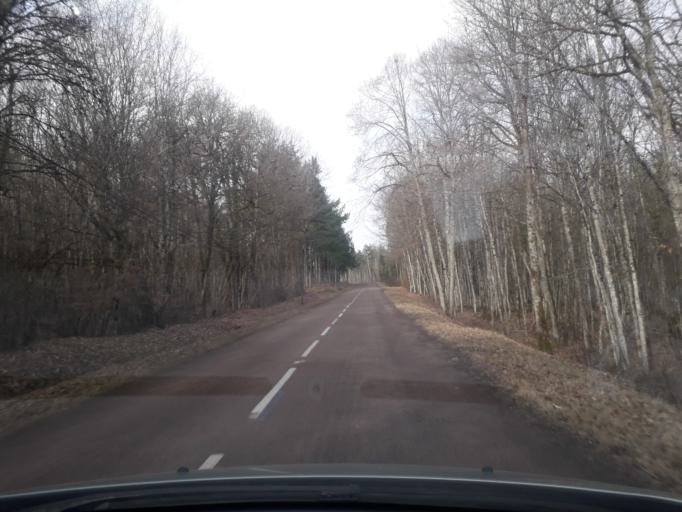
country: FR
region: Bourgogne
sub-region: Departement de la Cote-d'Or
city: Messigny-et-Vantoux
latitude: 47.4265
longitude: 5.0083
